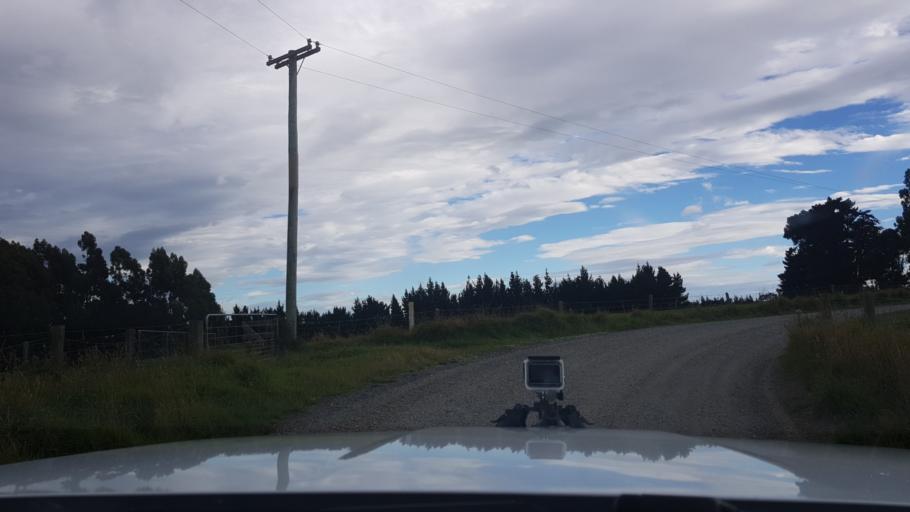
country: NZ
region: Otago
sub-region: Clutha District
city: Balclutha
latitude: -46.2127
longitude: 169.7369
